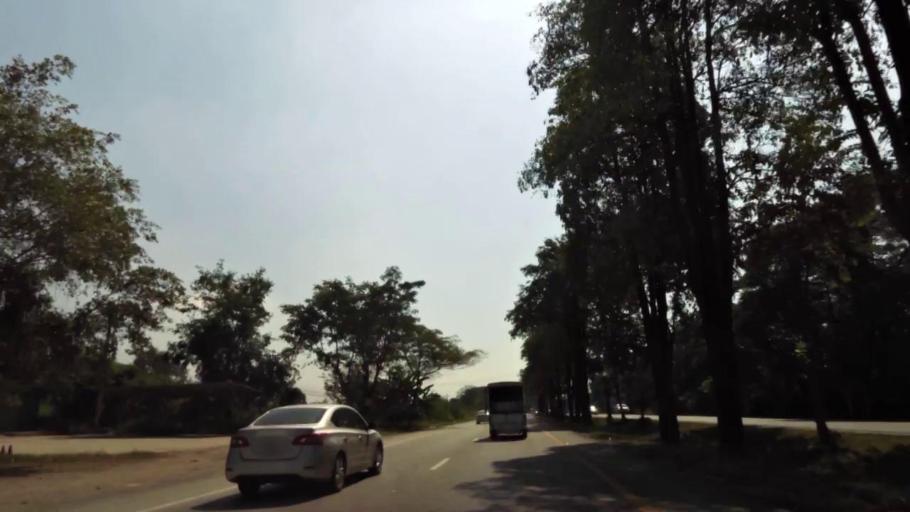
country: TH
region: Phichit
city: Bueng Na Rang
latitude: 16.1173
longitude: 100.1257
